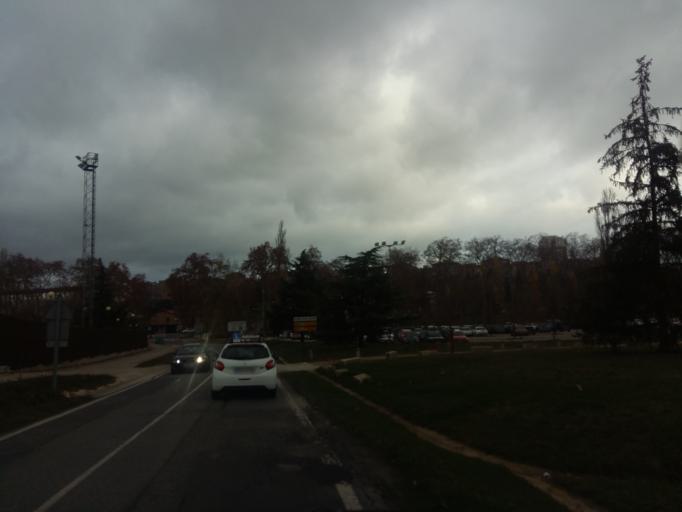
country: ES
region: Navarre
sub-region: Provincia de Navarra
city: Iturrama
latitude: 42.7978
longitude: -1.6531
